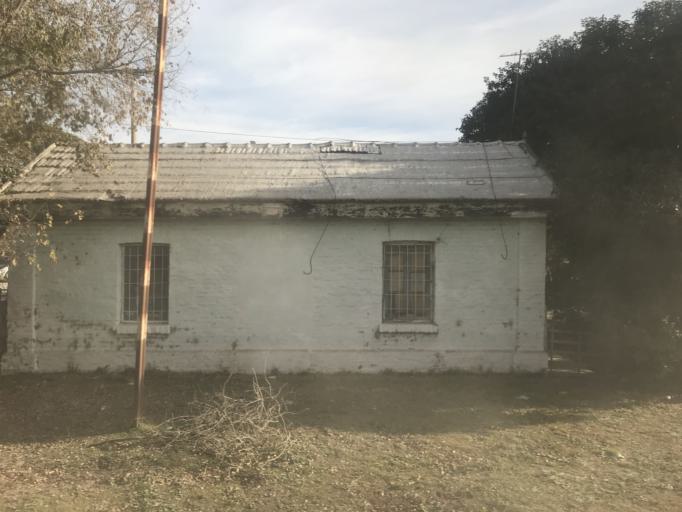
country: AR
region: Cordoba
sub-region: Departamento de Rio Segundo
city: Rio Segundo
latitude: -31.6560
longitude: -63.9084
